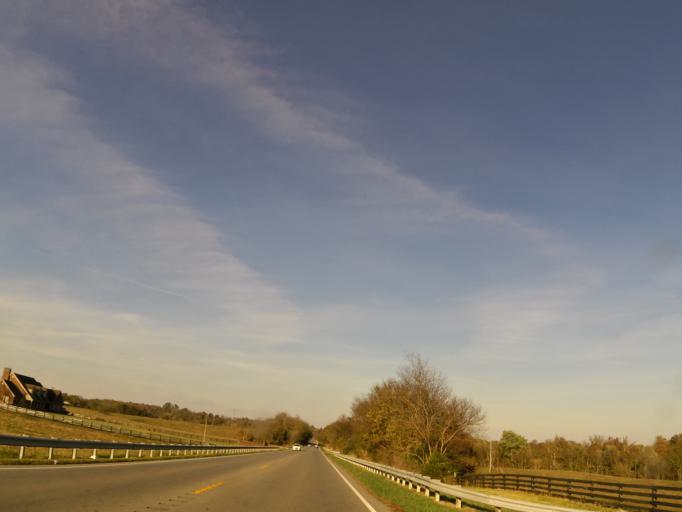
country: US
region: Kentucky
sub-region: Lincoln County
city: Stanford
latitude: 37.5623
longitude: -84.6247
